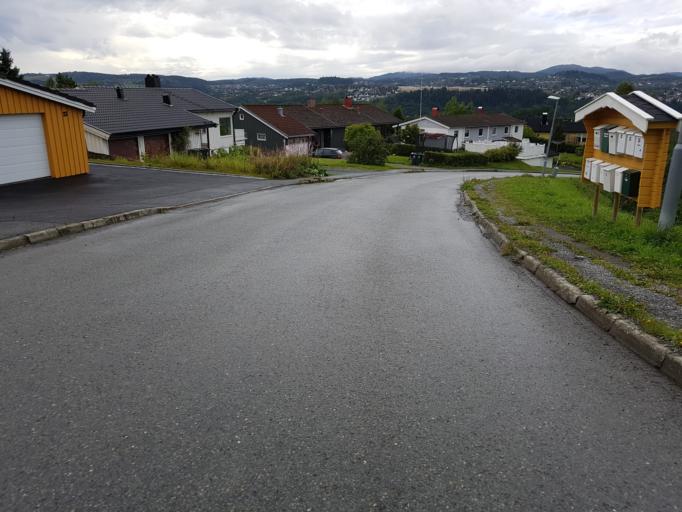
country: NO
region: Sor-Trondelag
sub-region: Trondheim
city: Trondheim
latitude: 63.3925
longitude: 10.4178
